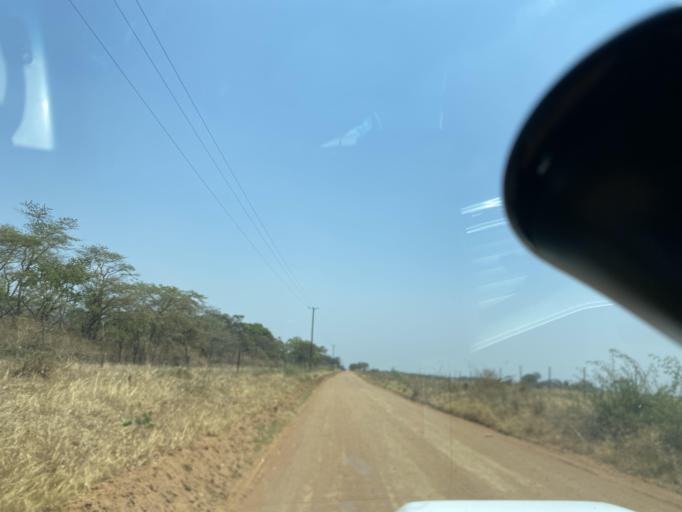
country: ZM
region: Lusaka
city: Lusaka
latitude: -15.4388
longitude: 28.0630
